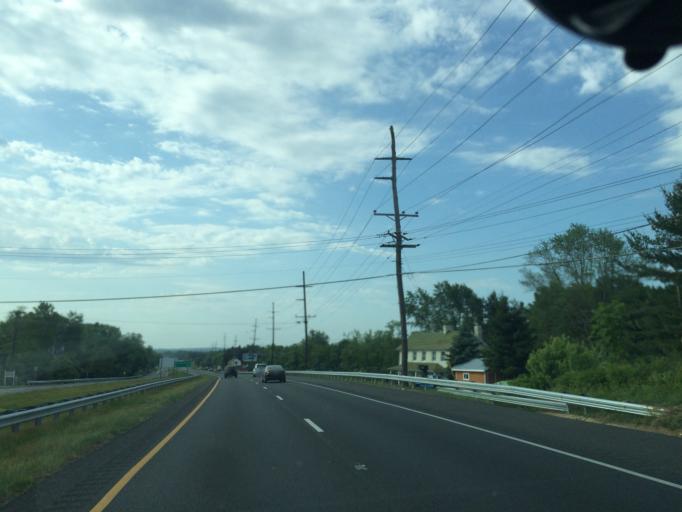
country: US
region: Maryland
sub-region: Baltimore County
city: Reisterstown
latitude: 39.5167
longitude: -76.9121
